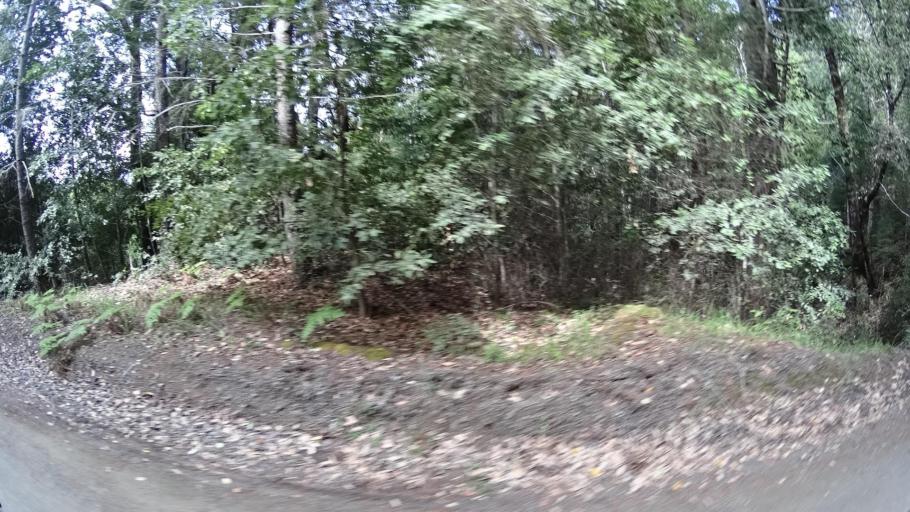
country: US
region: California
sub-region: Humboldt County
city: Redway
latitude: 40.0339
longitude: -123.8377
